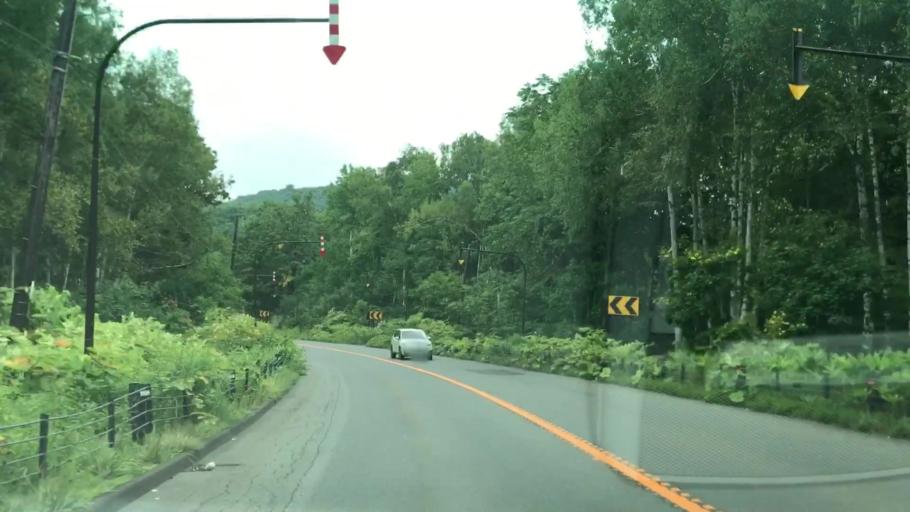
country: JP
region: Hokkaido
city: Otaru
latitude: 43.0068
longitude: 140.8768
